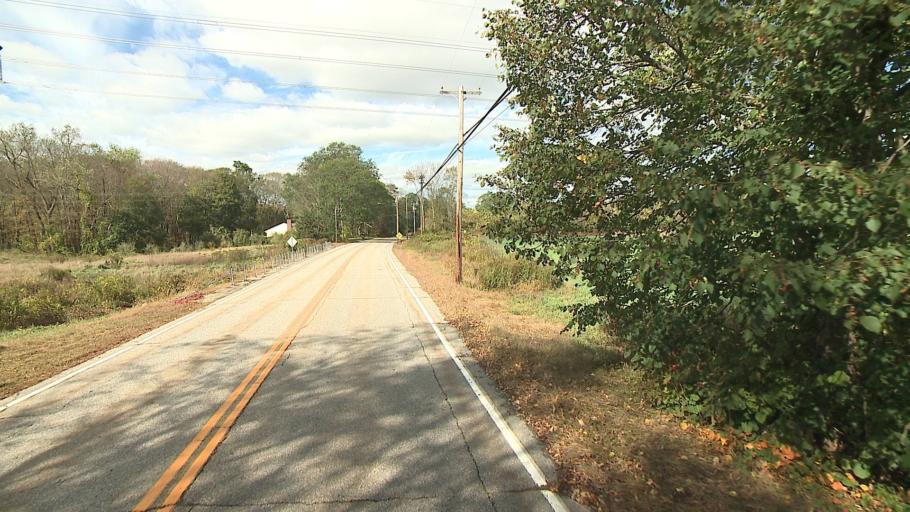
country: US
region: Connecticut
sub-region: Windham County
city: Putnam
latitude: 41.8957
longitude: -71.8814
